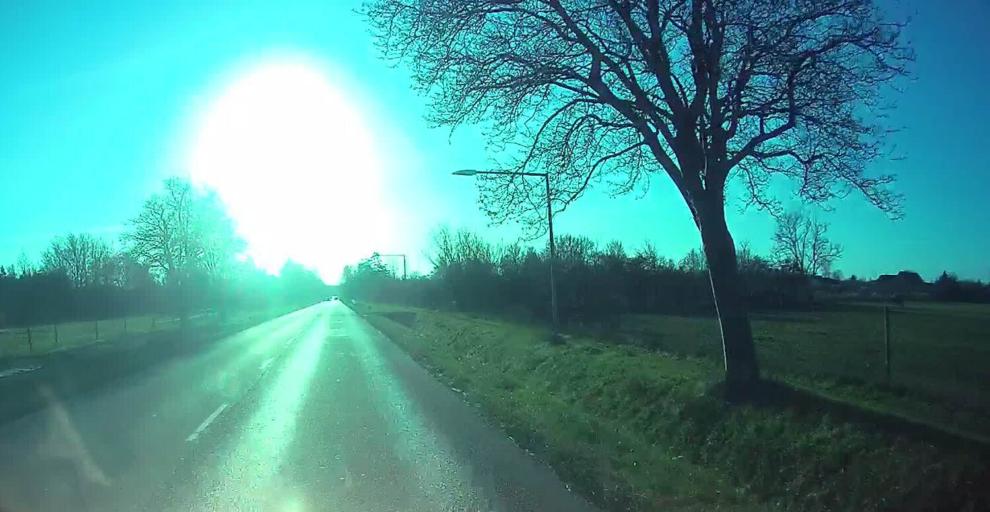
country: DK
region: Capital Region
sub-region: Tarnby Kommune
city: Tarnby
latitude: 55.5899
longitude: 12.5809
